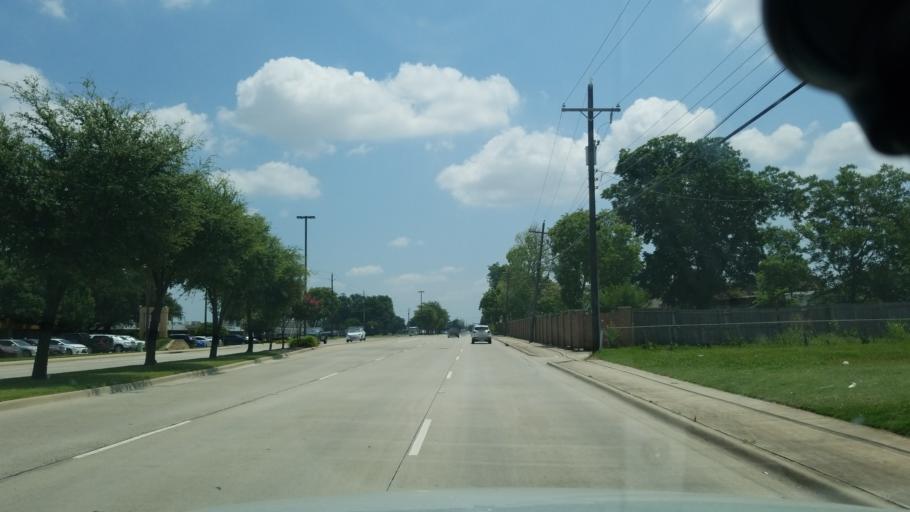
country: US
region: Texas
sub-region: Dallas County
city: Carrollton
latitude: 32.9535
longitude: -96.8765
